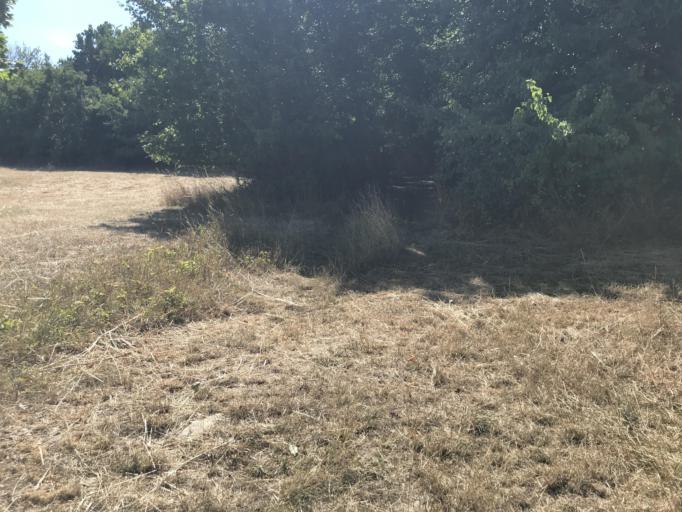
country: DE
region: Rheinland-Pfalz
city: Nieder-Olm
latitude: 49.9189
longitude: 8.2184
